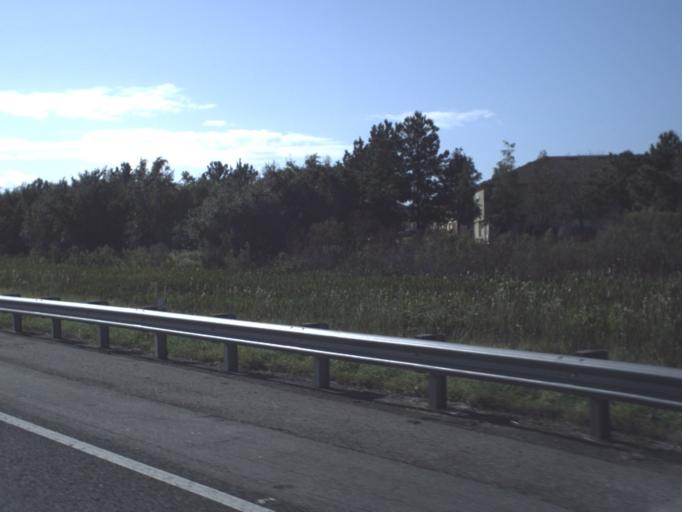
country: US
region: Florida
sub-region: Osceola County
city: Buenaventura Lakes
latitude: 28.2861
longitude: -81.3427
